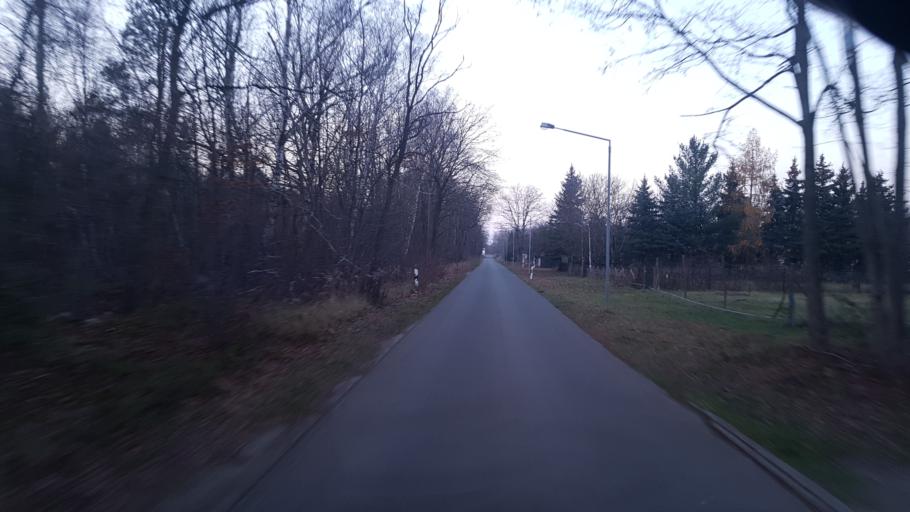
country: DE
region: Brandenburg
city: Lauchhammer
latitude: 51.5191
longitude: 13.7408
